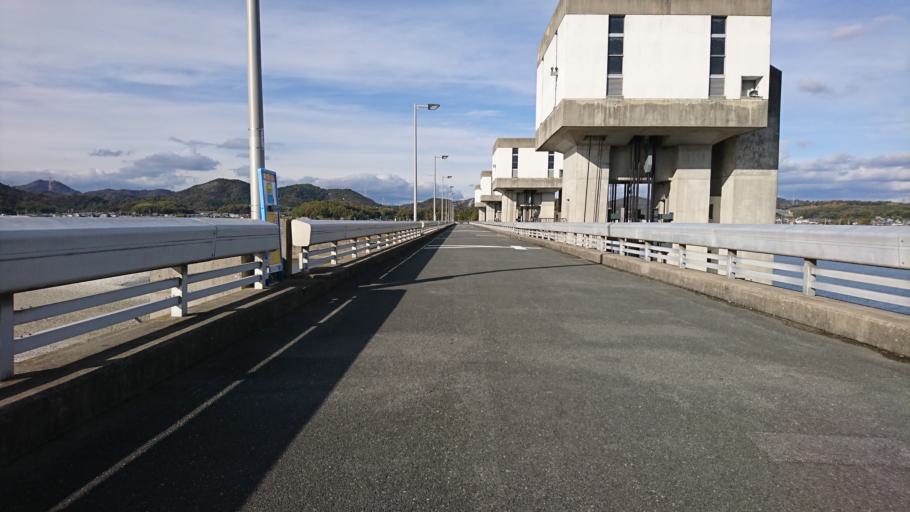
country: JP
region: Hyogo
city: Kakogawacho-honmachi
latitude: 34.7944
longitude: 134.8910
